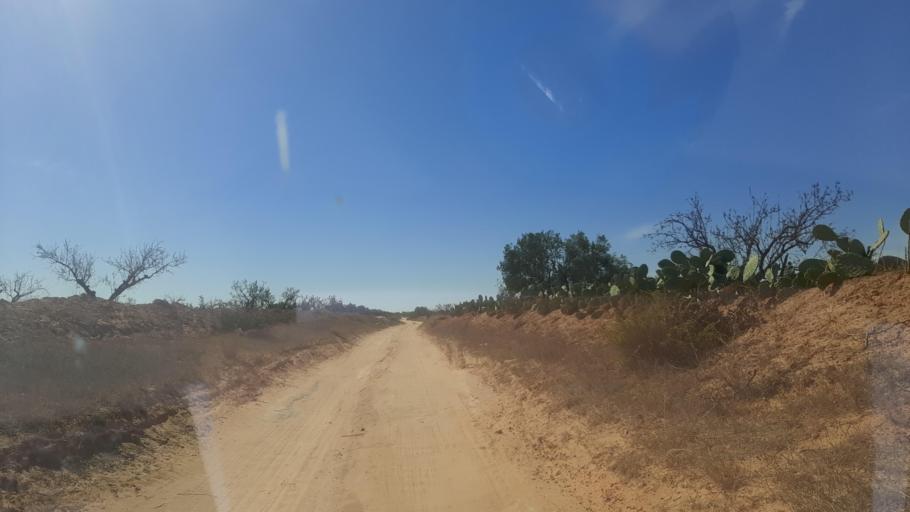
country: TN
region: Safaqis
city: Sfax
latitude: 34.8268
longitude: 10.5547
